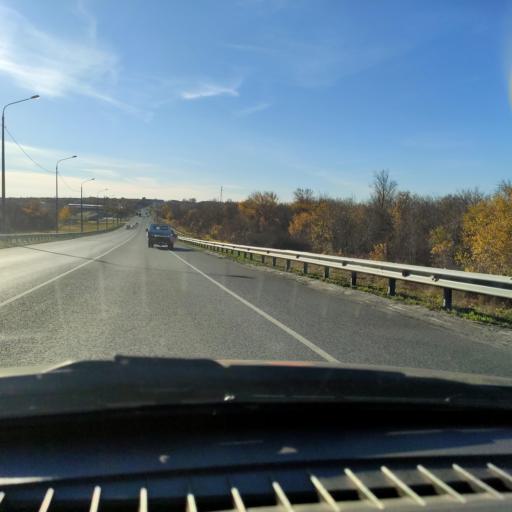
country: RU
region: Samara
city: Mezhdurechensk
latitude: 53.2529
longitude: 49.0356
